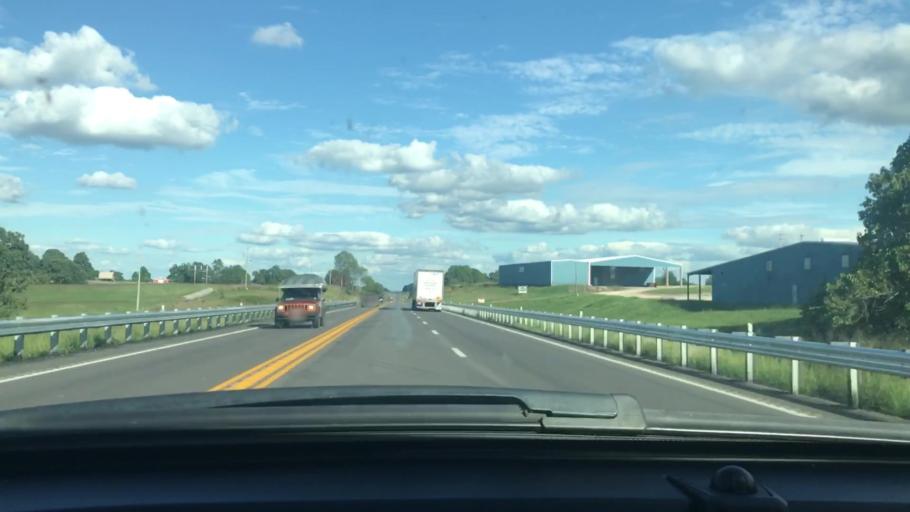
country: US
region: Missouri
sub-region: Oregon County
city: Thayer
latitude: 36.5883
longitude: -91.6355
